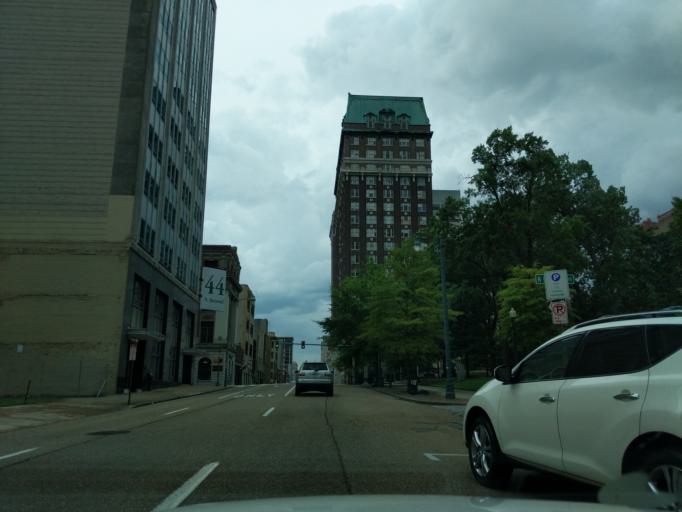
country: US
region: Tennessee
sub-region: Shelby County
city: Memphis
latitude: 35.1465
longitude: -90.0509
